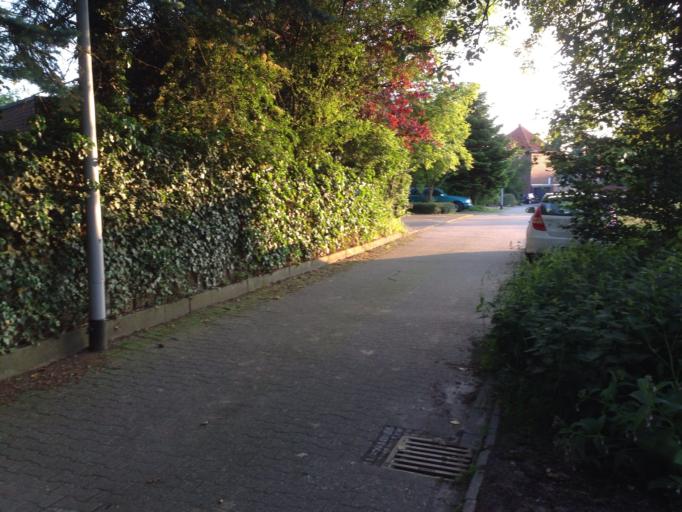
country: DE
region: North Rhine-Westphalia
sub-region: Regierungsbezirk Munster
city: Greven
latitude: 52.0203
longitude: 7.5618
